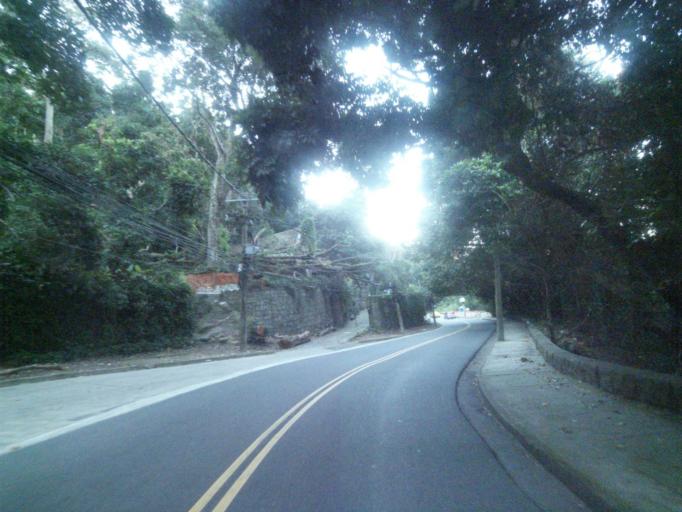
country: BR
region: Rio de Janeiro
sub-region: Rio De Janeiro
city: Rio de Janeiro
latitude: -23.0035
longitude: -43.2797
